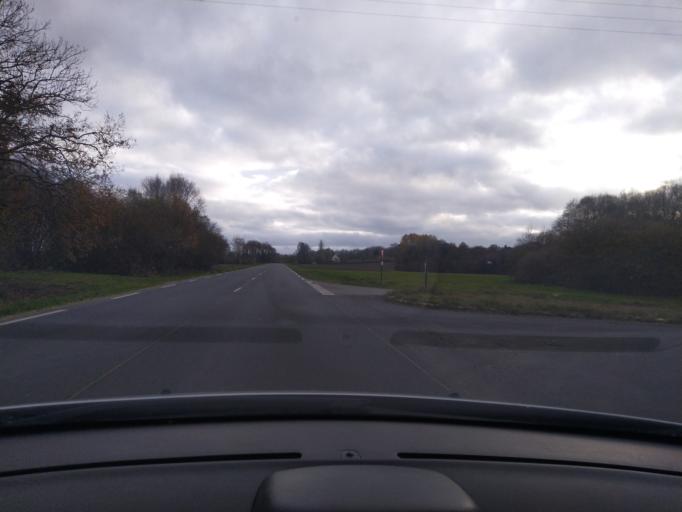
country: FR
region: Brittany
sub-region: Departement des Cotes-d'Armor
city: Plounevez-Moedec
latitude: 48.5722
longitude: -3.4951
